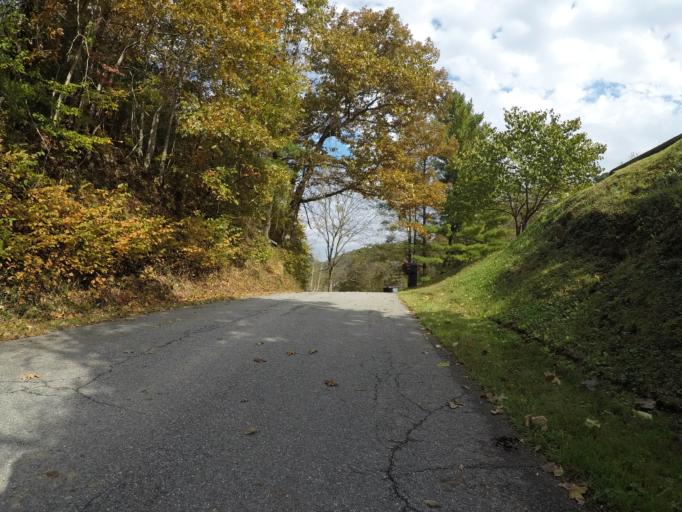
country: US
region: West Virginia
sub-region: Wayne County
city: Lavalette
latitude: 38.3482
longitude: -82.4422
